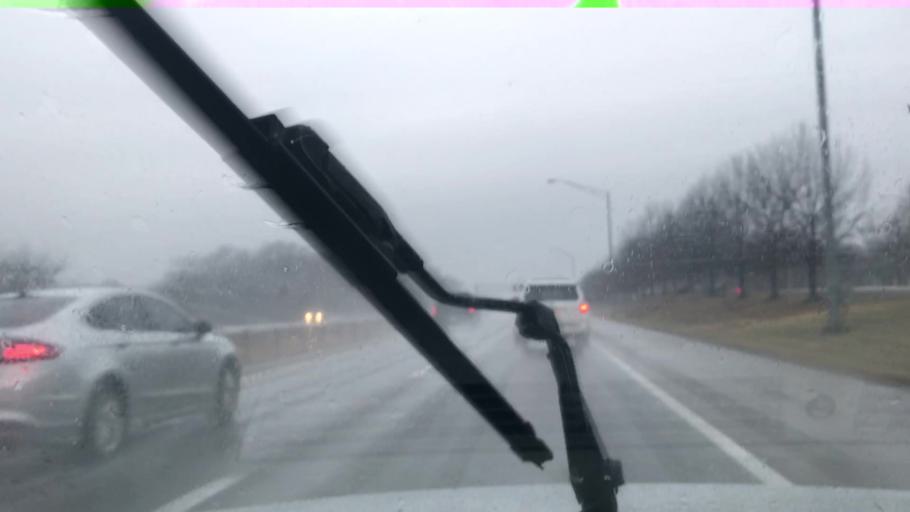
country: US
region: Kentucky
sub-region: Christian County
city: Oak Grove
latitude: 36.6481
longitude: -87.3497
